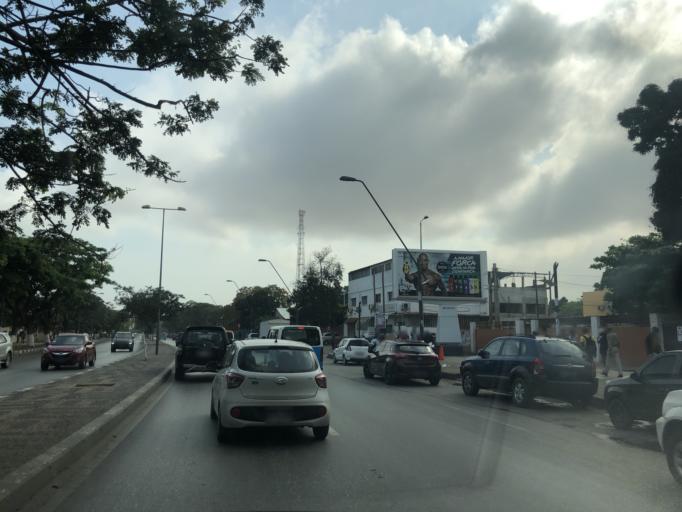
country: AO
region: Luanda
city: Luanda
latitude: -8.8371
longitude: 13.2371
